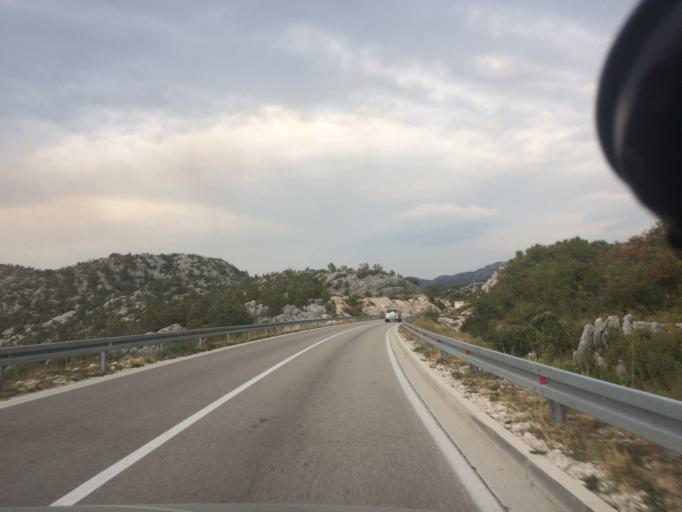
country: ME
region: Kotor
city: Risan
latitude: 42.6328
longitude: 18.6807
